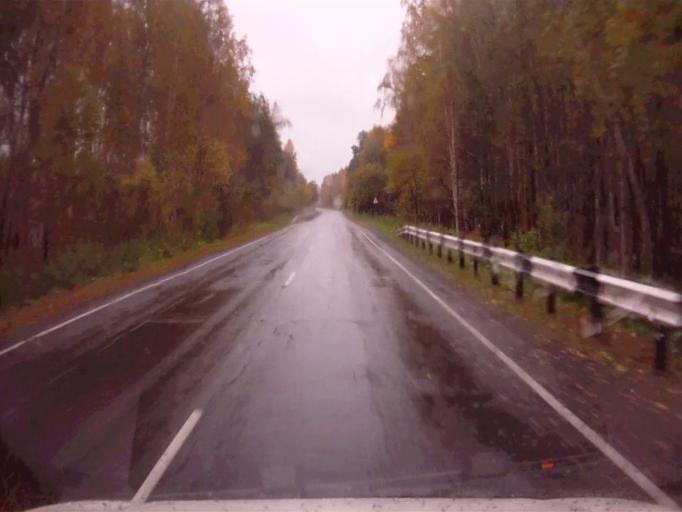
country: RU
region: Chelyabinsk
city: Verkhniy Ufaley
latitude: 55.9412
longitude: 60.4097
